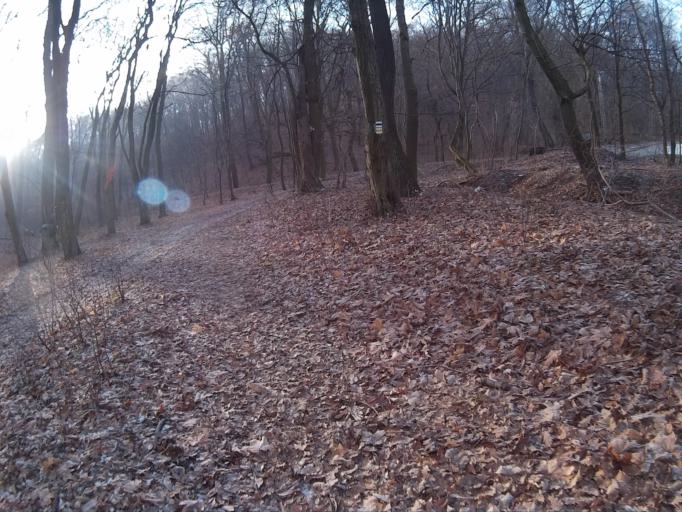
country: HU
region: Komarom-Esztergom
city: Oroszlany
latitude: 47.4697
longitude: 18.3946
